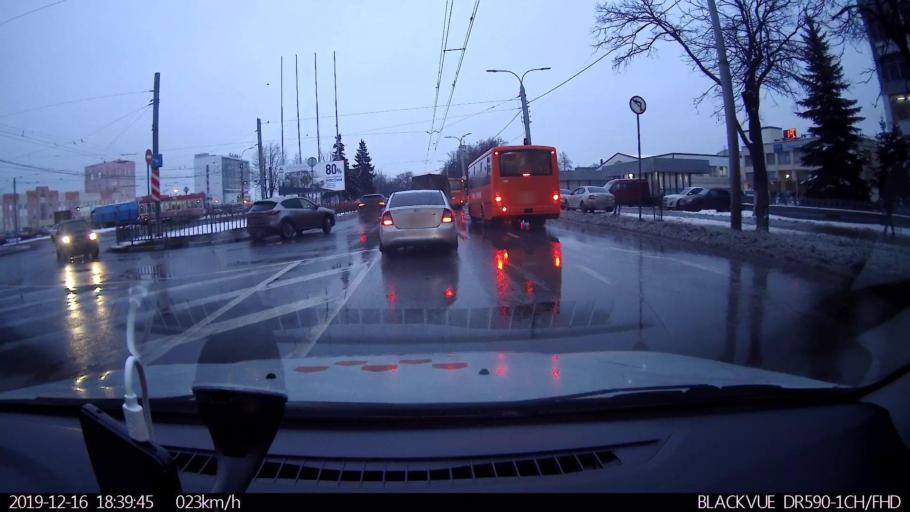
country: RU
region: Nizjnij Novgorod
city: Gorbatovka
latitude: 56.2465
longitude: 43.8754
